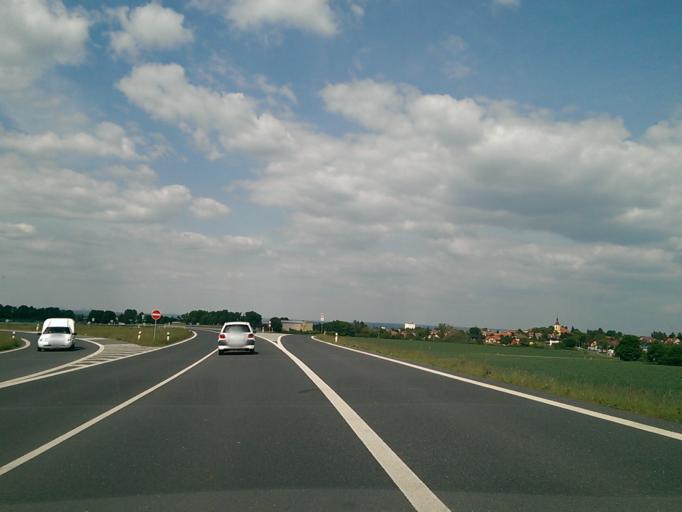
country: CZ
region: Central Bohemia
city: Libeznice
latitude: 50.1877
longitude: 14.4817
